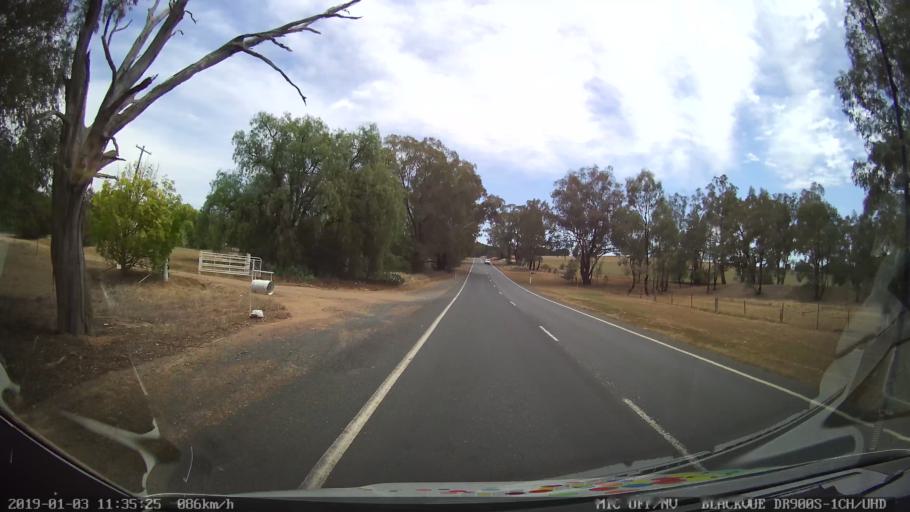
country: AU
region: New South Wales
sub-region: Weddin
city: Grenfell
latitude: -33.9225
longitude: 148.1596
